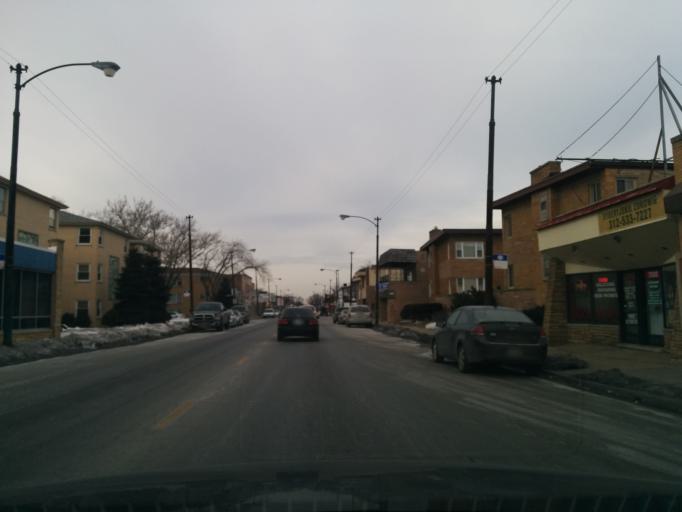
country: US
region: Illinois
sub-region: Cook County
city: Elmwood Park
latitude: 41.9381
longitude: -87.8016
